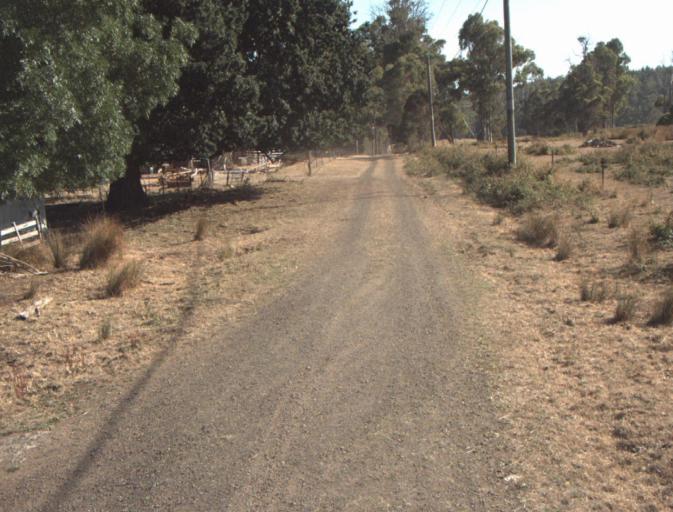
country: AU
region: Tasmania
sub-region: Dorset
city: Bridport
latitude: -41.1429
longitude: 147.2124
